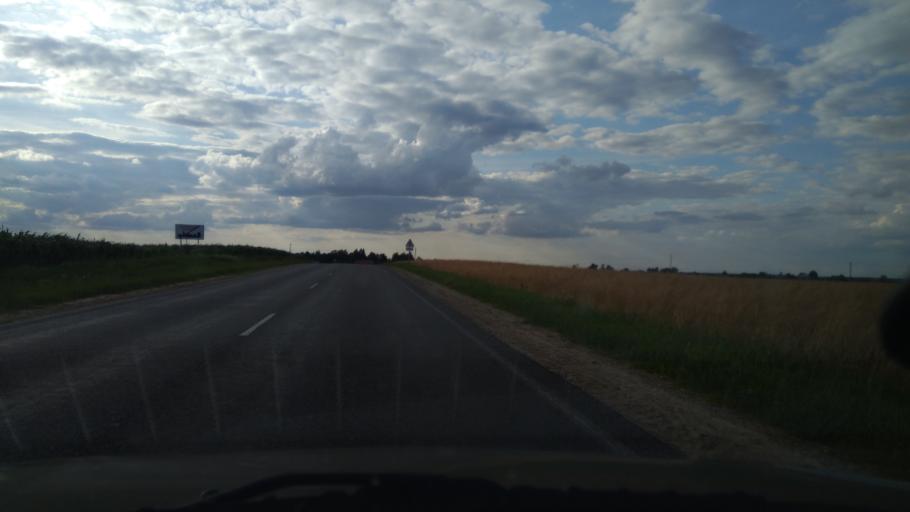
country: BY
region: Grodnenskaya
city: Masty
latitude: 53.3138
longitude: 24.6936
